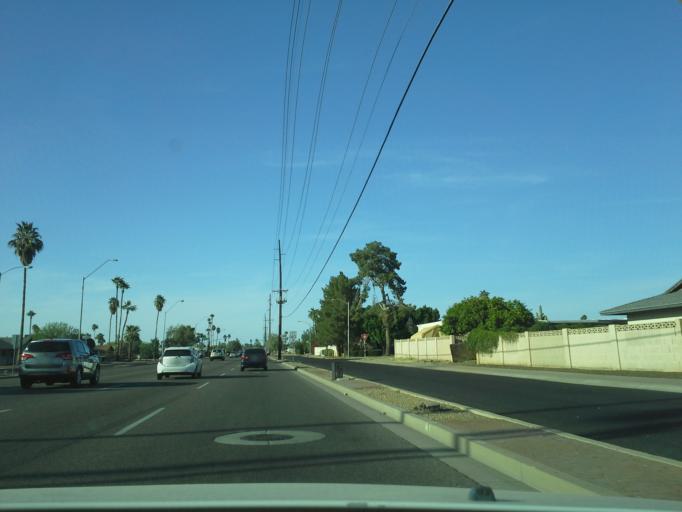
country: US
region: Arizona
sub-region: Maricopa County
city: Glendale
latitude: 33.6152
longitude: -112.1337
